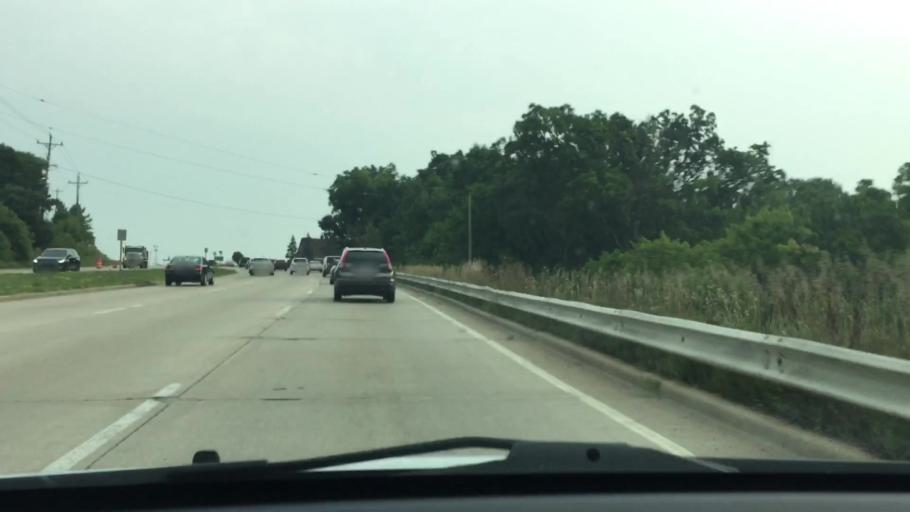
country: US
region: Wisconsin
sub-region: Waukesha County
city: Waukesha
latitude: 42.9984
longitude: -88.1999
